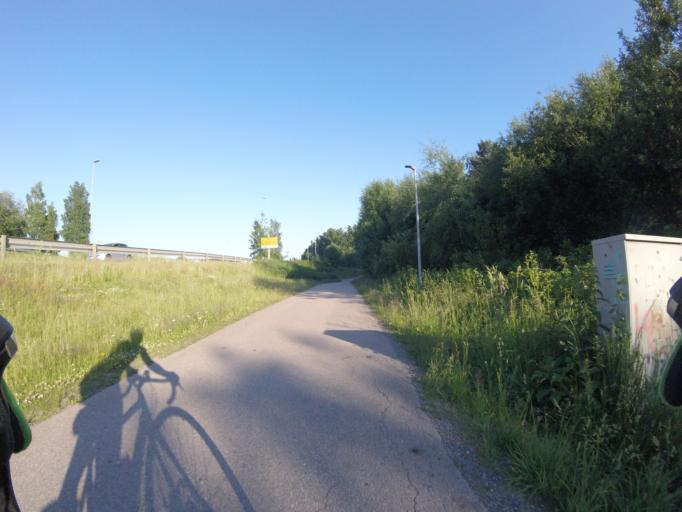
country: NO
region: Akershus
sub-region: Skedsmo
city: Lillestrom
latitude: 59.9637
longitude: 11.0581
